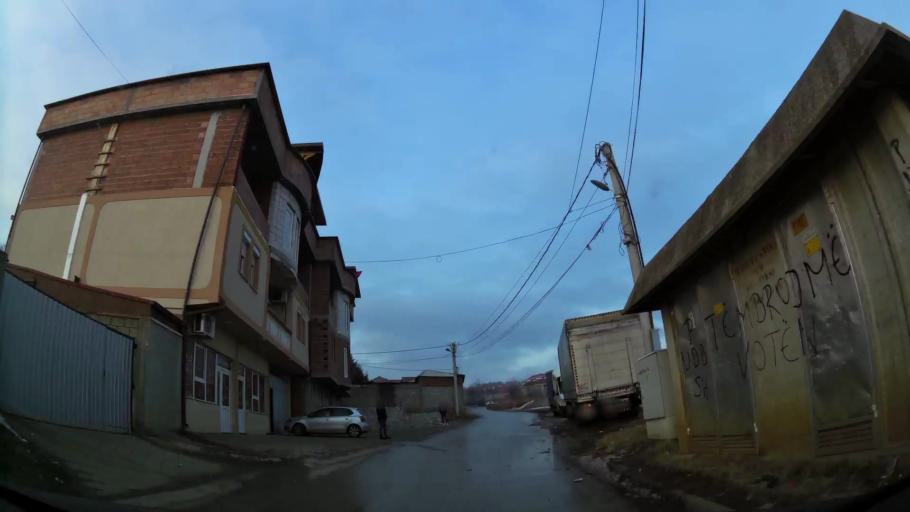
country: MK
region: Aracinovo
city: Arachinovo
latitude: 42.0249
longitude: 21.5724
